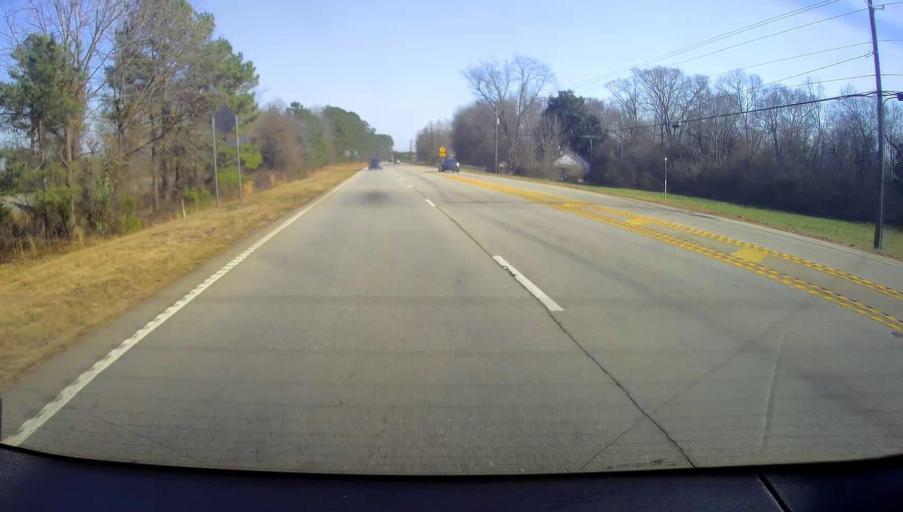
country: US
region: Georgia
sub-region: Butts County
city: Jackson
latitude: 33.3187
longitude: -83.9890
